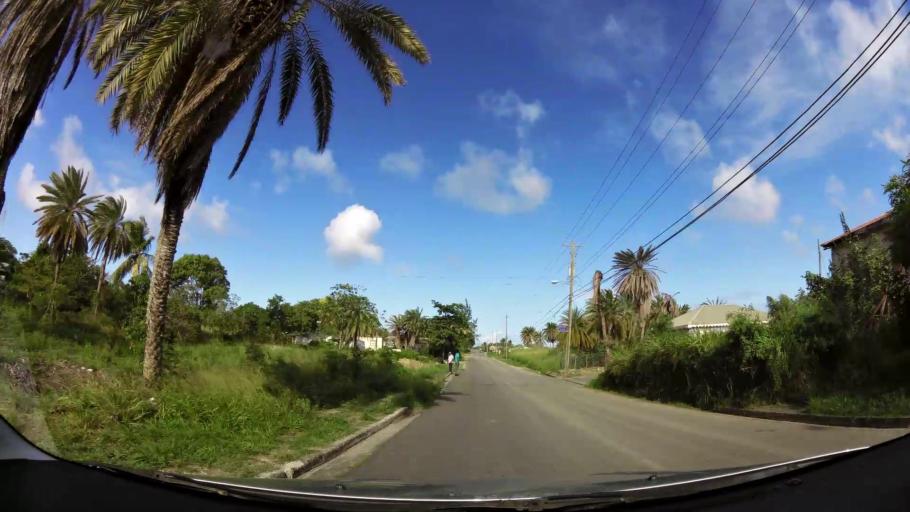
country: AG
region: Saint Peter
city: All Saints
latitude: 17.0689
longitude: -61.7913
